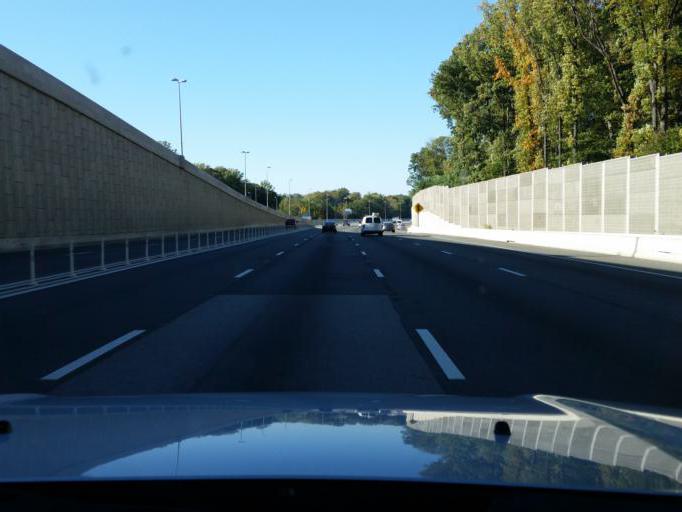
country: US
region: Virginia
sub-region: Fairfax County
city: Ravensworth
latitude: 38.8137
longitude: -77.2192
